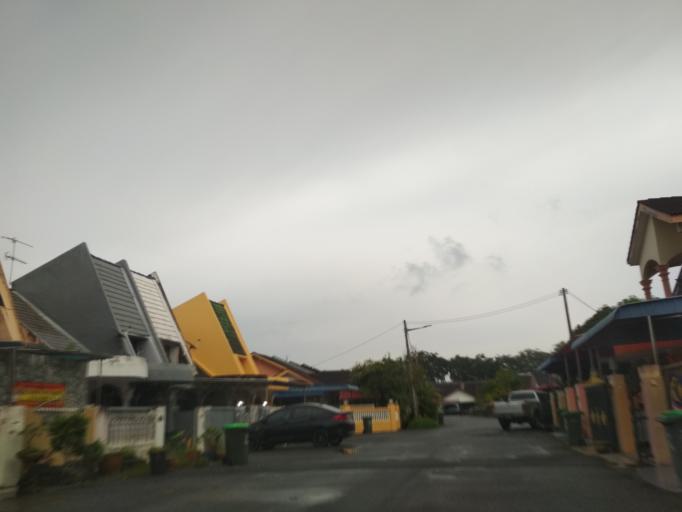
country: MY
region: Perlis
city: Kangar
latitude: 6.4476
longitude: 100.2073
